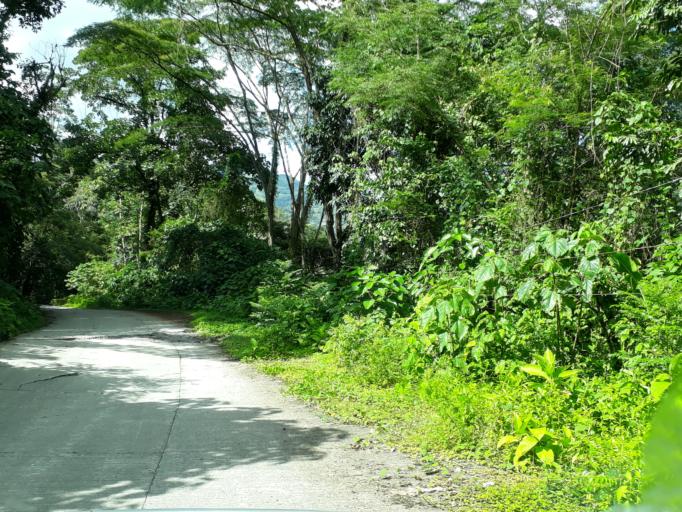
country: CO
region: Boyaca
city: Santa Maria
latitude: 4.7436
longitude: -73.3366
